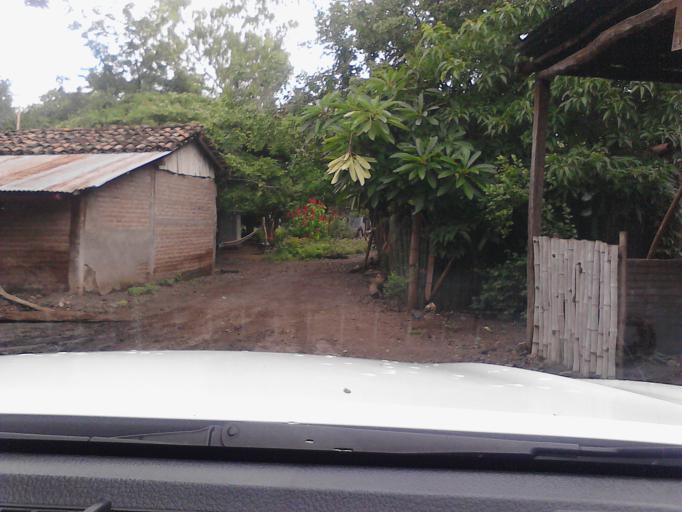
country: NI
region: Matagalpa
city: Ciudad Dario
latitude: 12.8978
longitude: -86.1303
